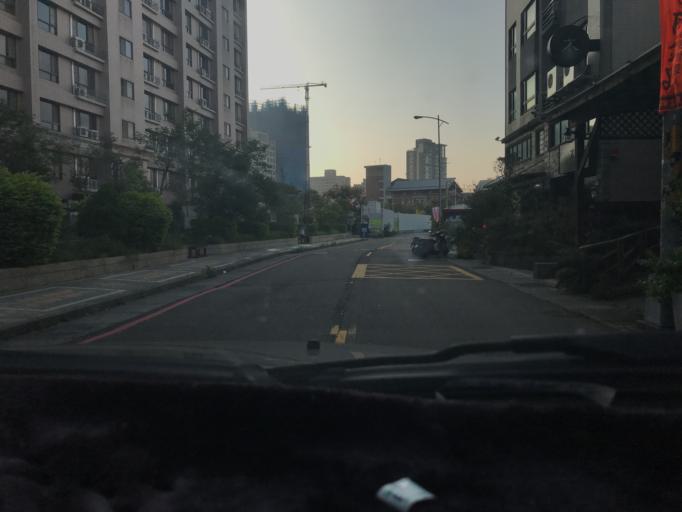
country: TW
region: Taiwan
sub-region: Hsinchu
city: Zhubei
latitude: 24.8139
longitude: 121.0355
